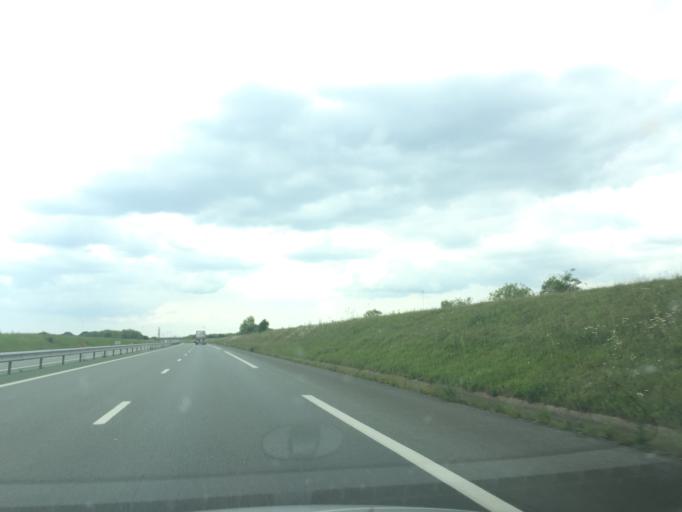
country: FR
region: Poitou-Charentes
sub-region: Departement des Deux-Sevres
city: Villiers-en-Plaine
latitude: 46.4172
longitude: -0.5627
